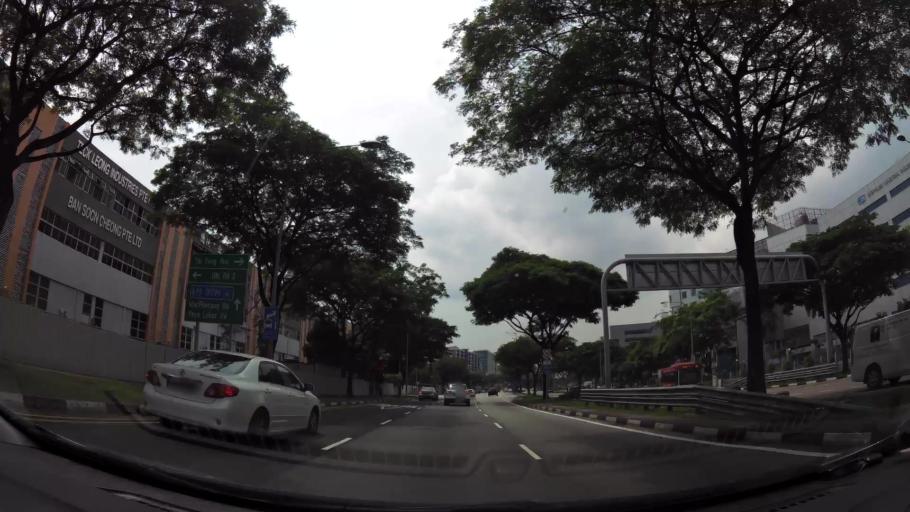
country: SG
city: Singapore
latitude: 1.3366
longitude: 103.8952
